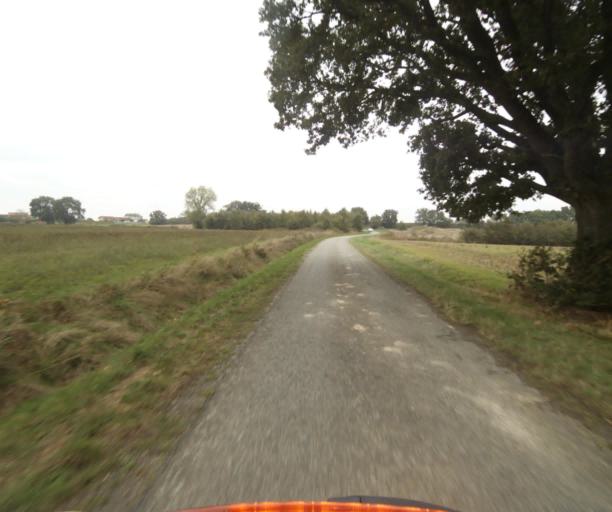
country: FR
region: Midi-Pyrenees
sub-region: Departement du Tarn-et-Garonne
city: Verdun-sur-Garonne
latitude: 43.8174
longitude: 1.2065
